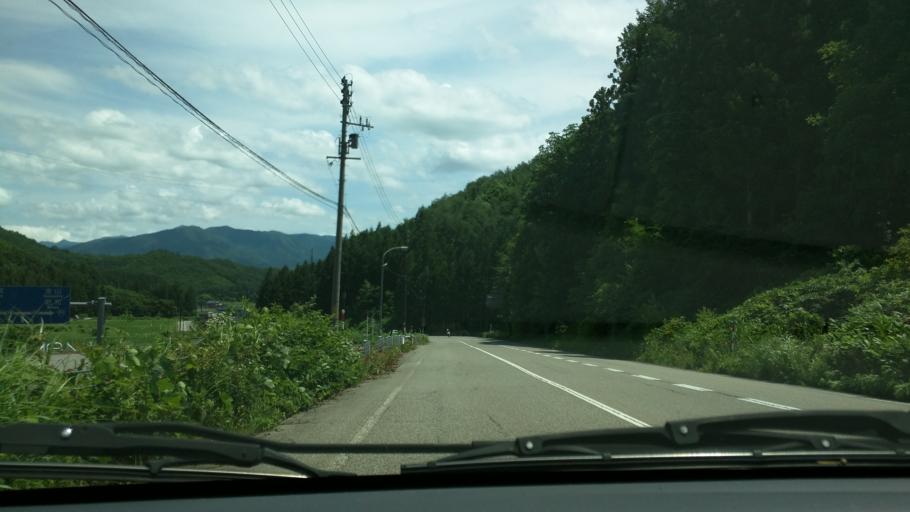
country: JP
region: Tochigi
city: Kuroiso
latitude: 37.2261
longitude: 139.7394
